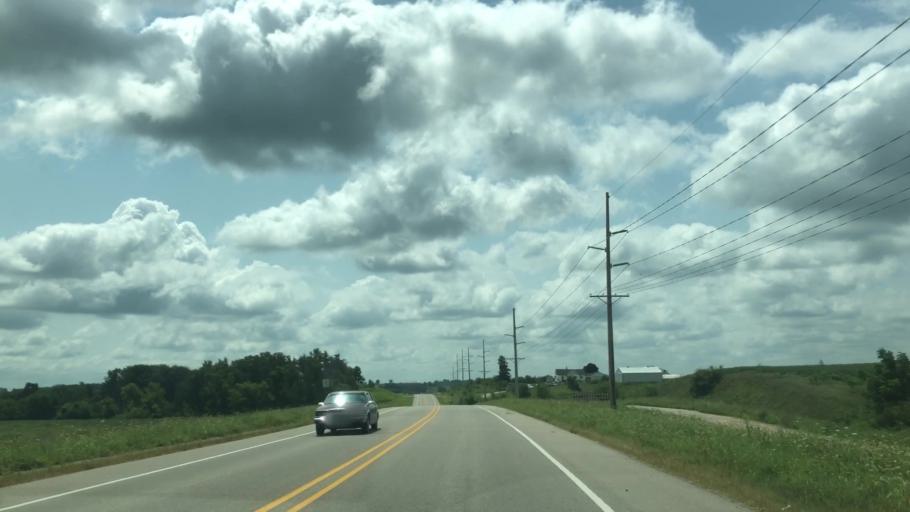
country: US
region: Iowa
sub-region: Marshall County
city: Marshalltown
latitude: 42.0300
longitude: -92.9604
